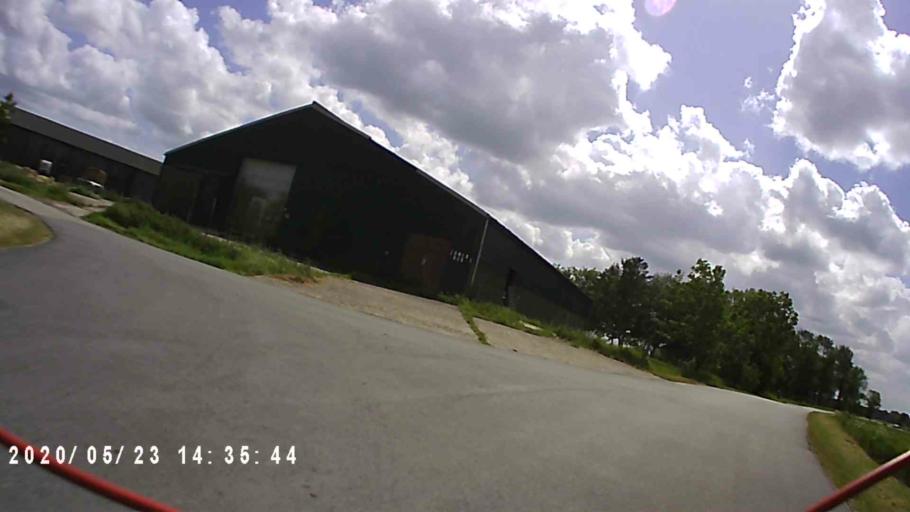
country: NL
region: Groningen
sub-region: Gemeente Delfzijl
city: Delfzijl
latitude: 53.2722
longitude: 6.9632
